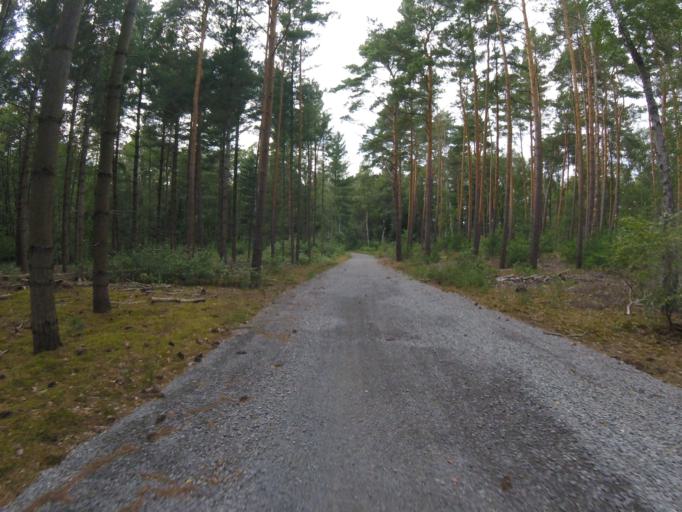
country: DE
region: Brandenburg
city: Halbe
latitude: 52.1517
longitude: 13.7477
